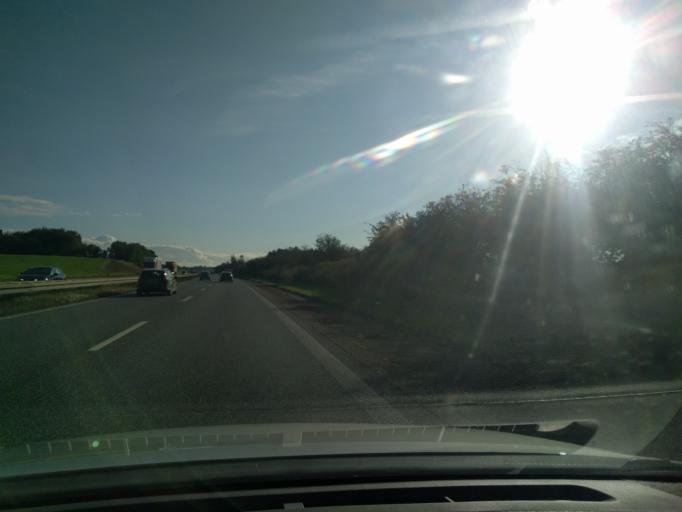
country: DK
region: Zealand
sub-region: Soro Kommune
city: Frederiksberg
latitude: 55.4523
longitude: 11.5960
